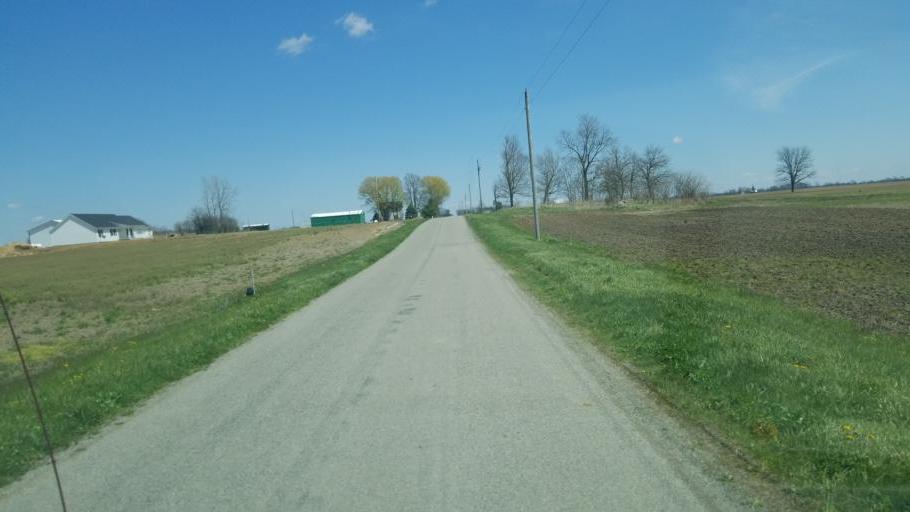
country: US
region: Ohio
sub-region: Union County
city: Richwood
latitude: 40.4918
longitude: -83.2785
